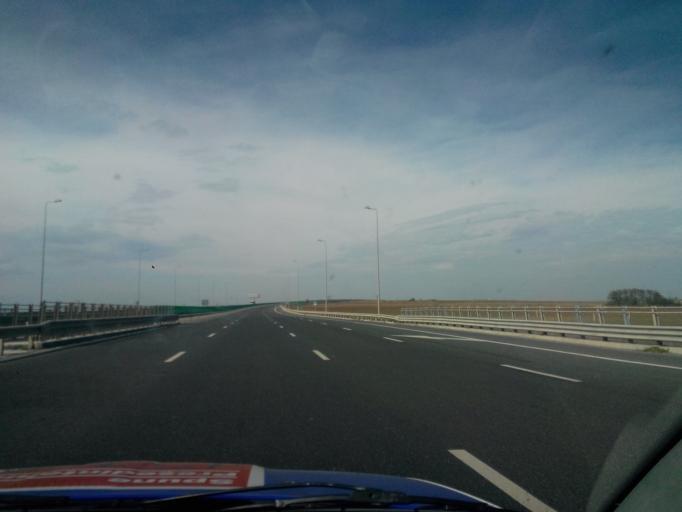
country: RO
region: Constanta
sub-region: Comuna Agigea
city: Agigea
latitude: 44.1085
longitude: 28.6014
